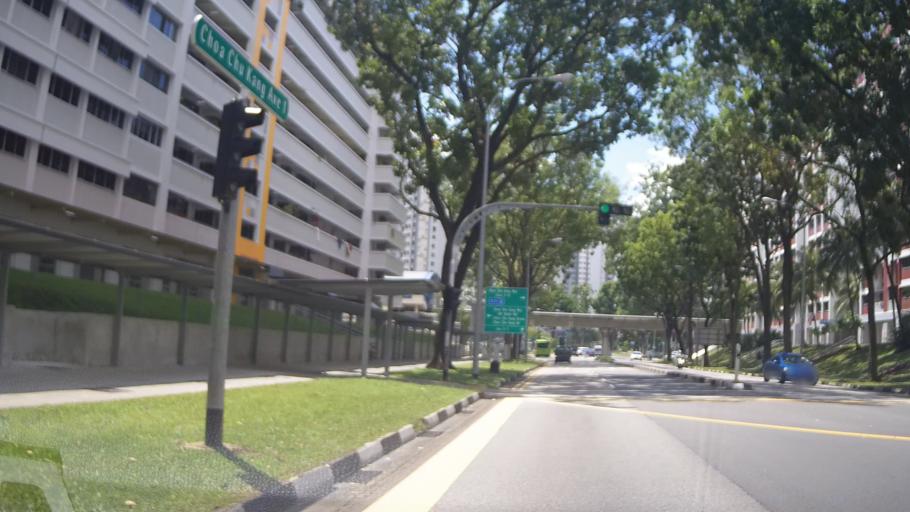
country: MY
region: Johor
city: Johor Bahru
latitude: 1.3801
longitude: 103.7493
